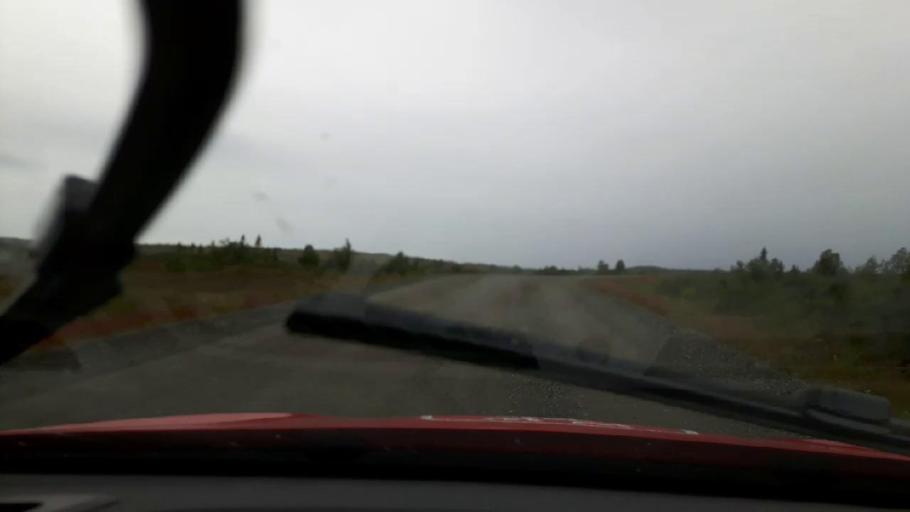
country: NO
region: Nord-Trondelag
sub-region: Meraker
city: Meraker
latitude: 63.6263
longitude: 12.2890
